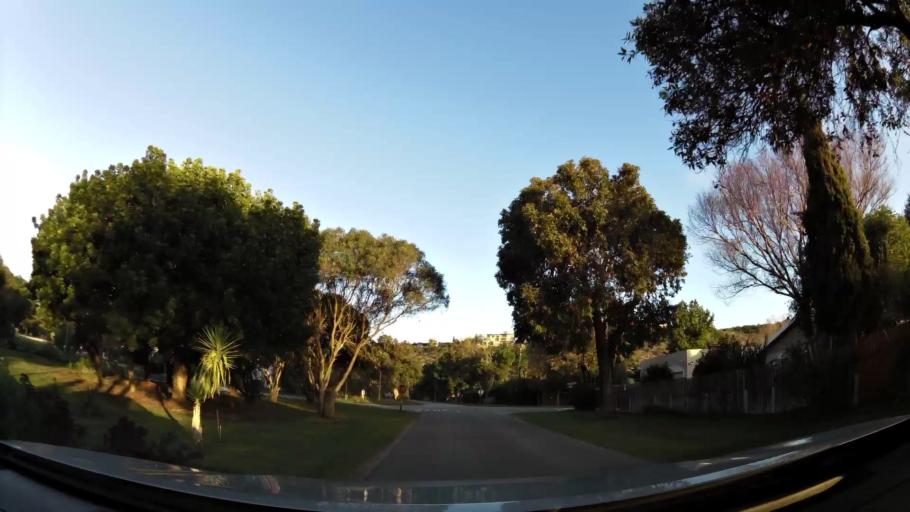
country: ZA
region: Western Cape
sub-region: Eden District Municipality
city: Knysna
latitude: -34.0197
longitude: 22.8048
